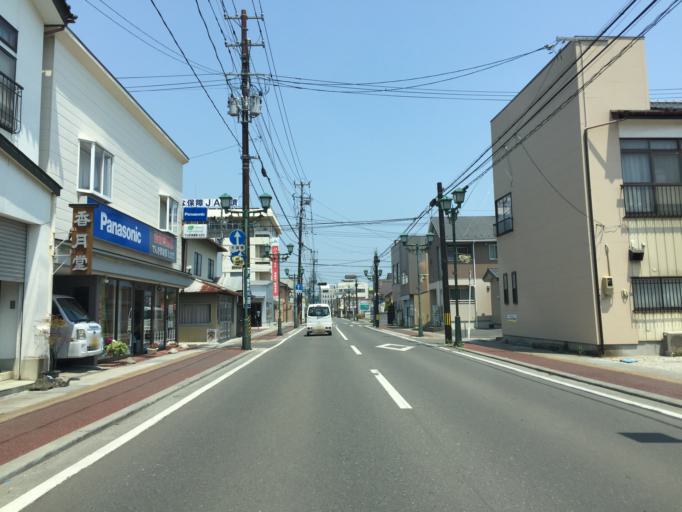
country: JP
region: Miyagi
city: Marumori
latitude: 37.7999
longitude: 140.9244
